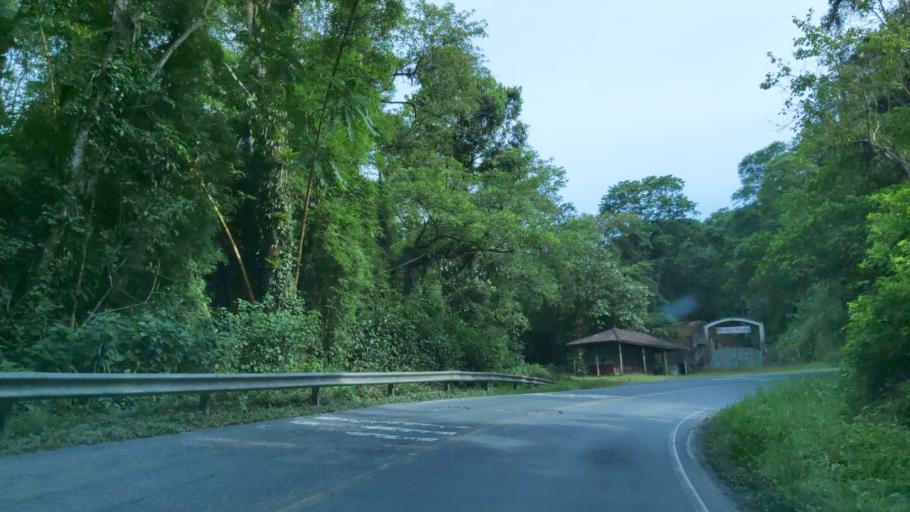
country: BR
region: Sao Paulo
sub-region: Juquia
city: Juquia
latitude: -24.1073
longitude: -47.6286
